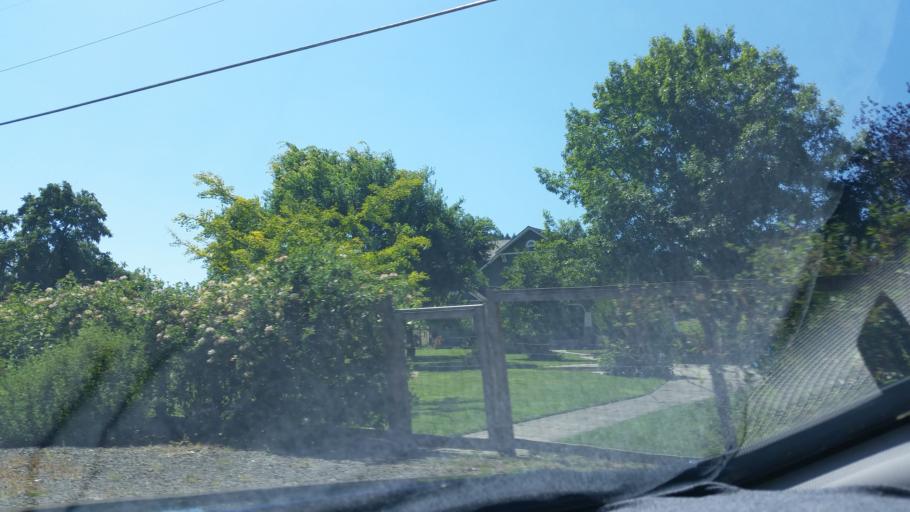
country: US
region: Oregon
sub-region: Clackamas County
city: Wilsonville
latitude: 45.2577
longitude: -122.8425
